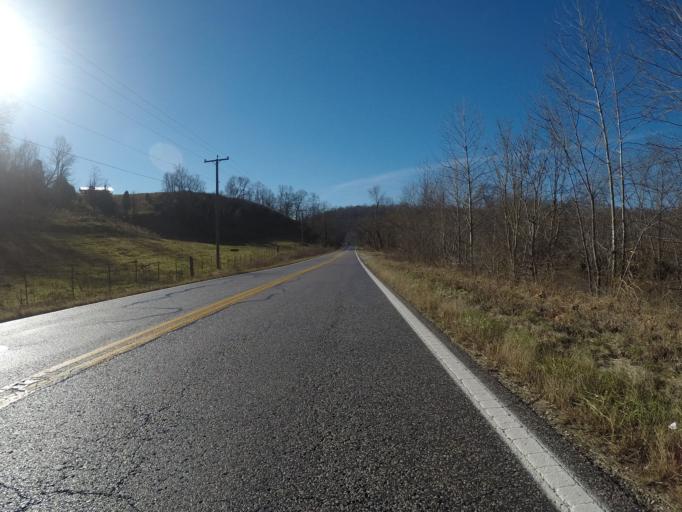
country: US
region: West Virginia
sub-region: Cabell County
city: Huntington
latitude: 38.4721
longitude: -82.4441
